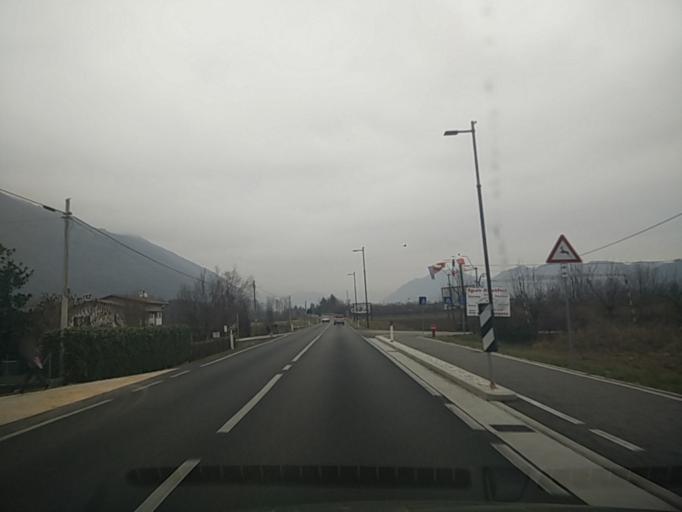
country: IT
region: Veneto
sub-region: Provincia di Treviso
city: Tarzo
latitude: 45.9780
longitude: 12.1939
